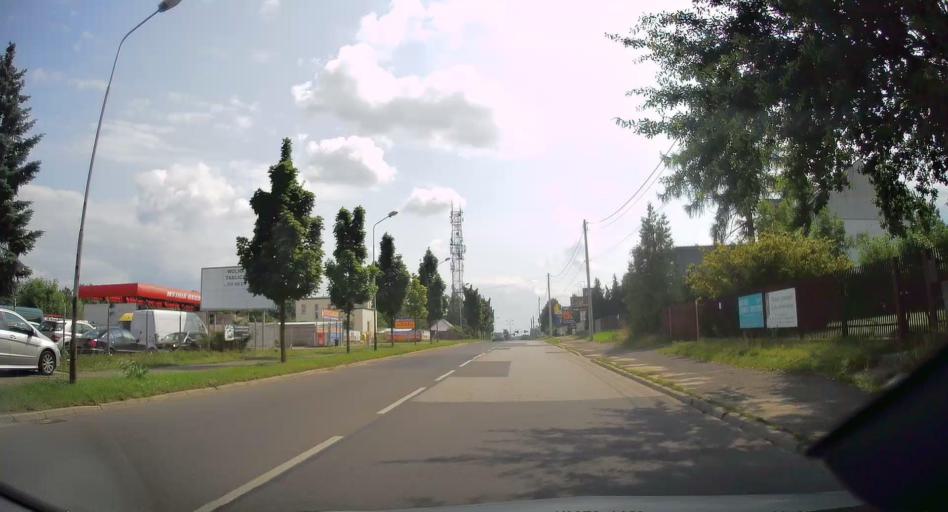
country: PL
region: Silesian Voivodeship
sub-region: Czestochowa
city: Czestochowa
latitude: 50.8164
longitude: 19.0852
